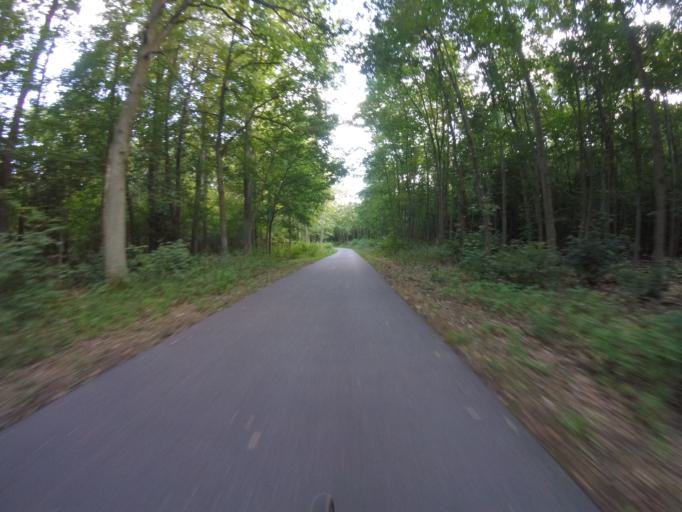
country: DE
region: Brandenburg
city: Petershagen
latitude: 52.5560
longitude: 13.8175
